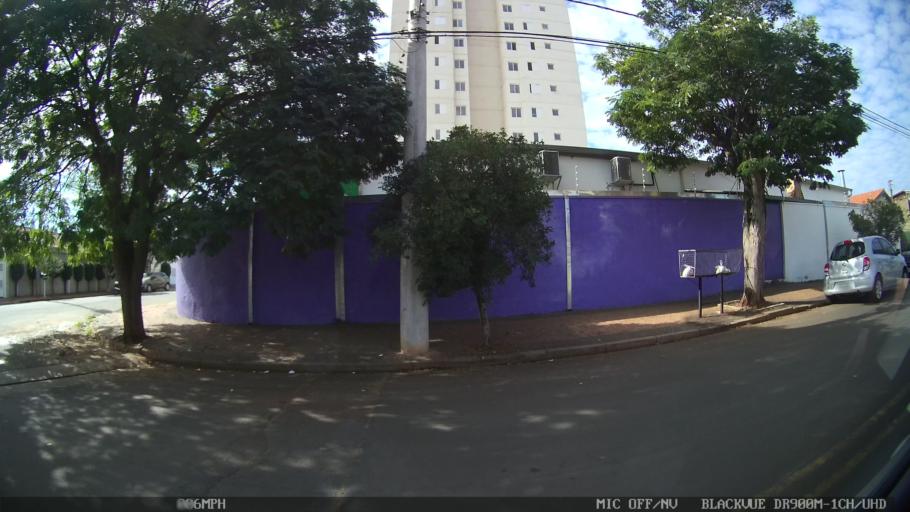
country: BR
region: Sao Paulo
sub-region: Santa Barbara D'Oeste
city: Santa Barbara d'Oeste
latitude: -22.7621
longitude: -47.4026
